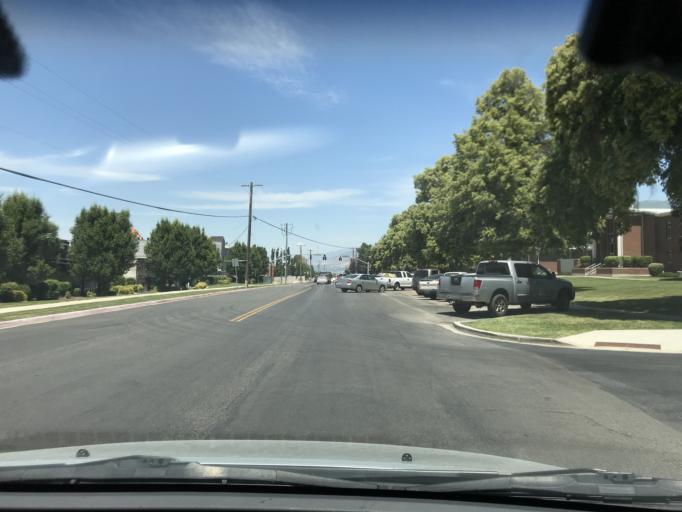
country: US
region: Utah
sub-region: Davis County
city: Woods Cross
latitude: 40.8604
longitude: -111.8922
